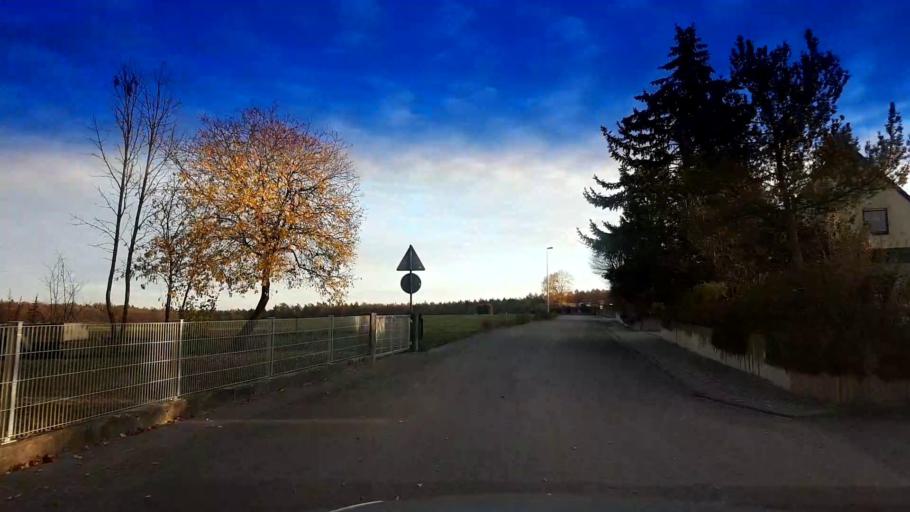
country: DE
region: Bavaria
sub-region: Upper Franconia
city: Priesendorf
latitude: 49.8797
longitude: 10.7312
